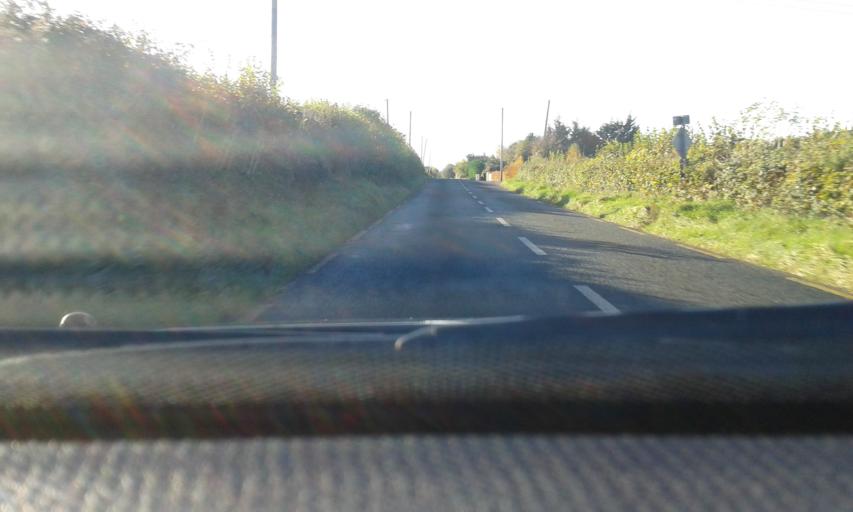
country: IE
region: Leinster
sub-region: Kildare
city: Monasterevin
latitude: 53.1705
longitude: -7.0299
